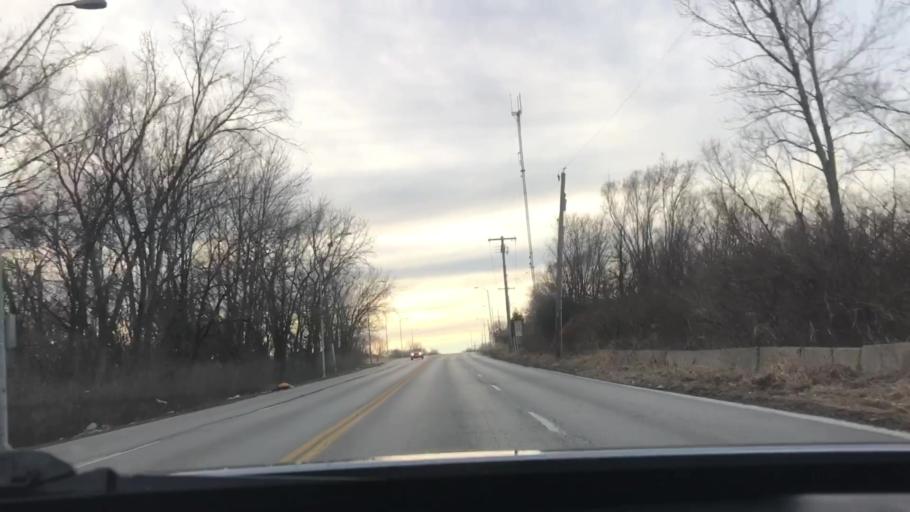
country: US
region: Missouri
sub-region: Jackson County
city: Sugar Creek
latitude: 39.0829
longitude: -94.5036
